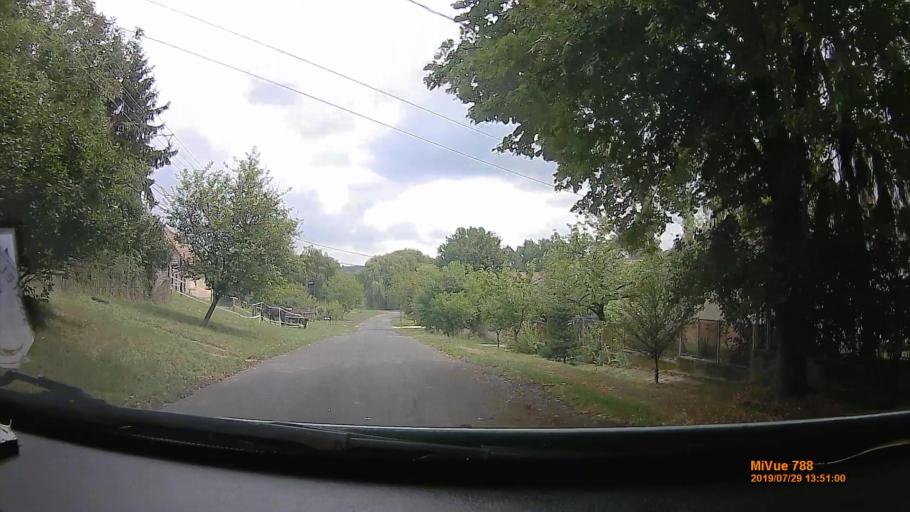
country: HU
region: Somogy
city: Tab
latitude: 46.7757
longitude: 17.9581
